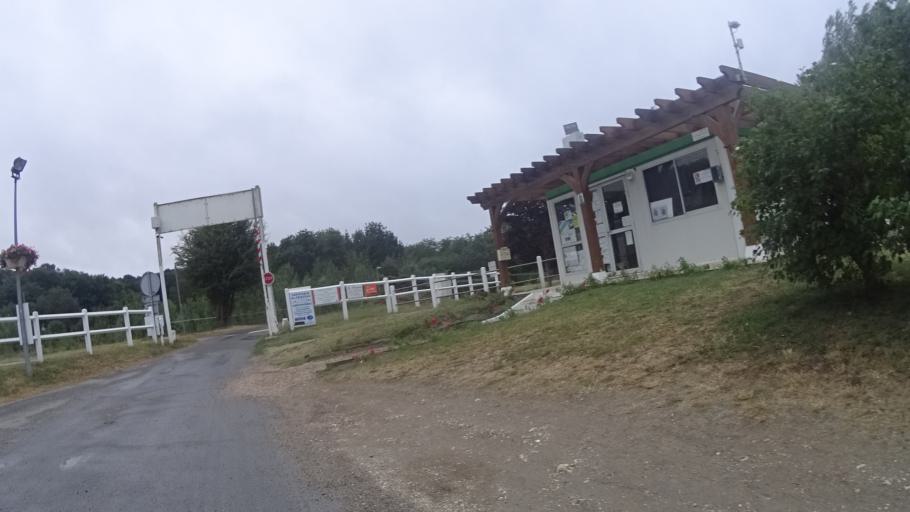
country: FR
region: Centre
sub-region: Departement du Loir-et-Cher
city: Chaumont-sur-Loire
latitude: 47.4848
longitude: 1.1943
